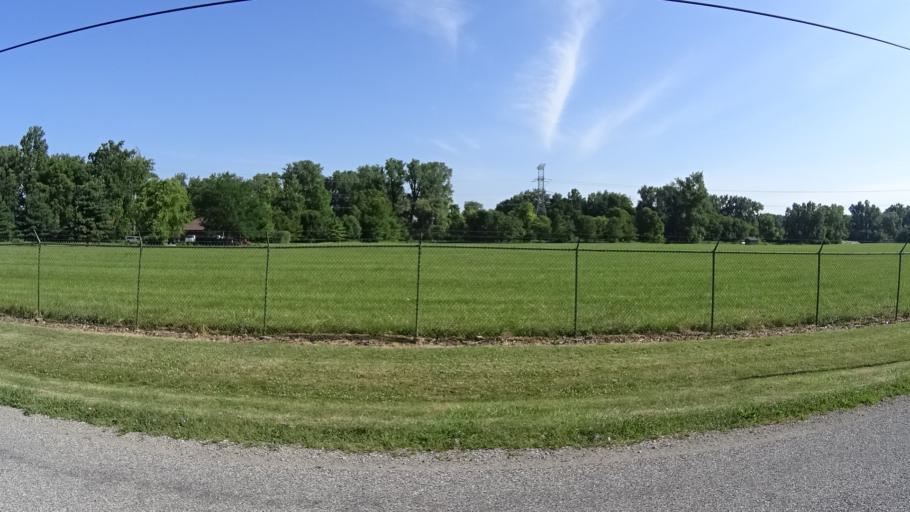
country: US
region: Ohio
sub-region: Huron County
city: Bellevue
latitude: 41.3872
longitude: -82.8385
